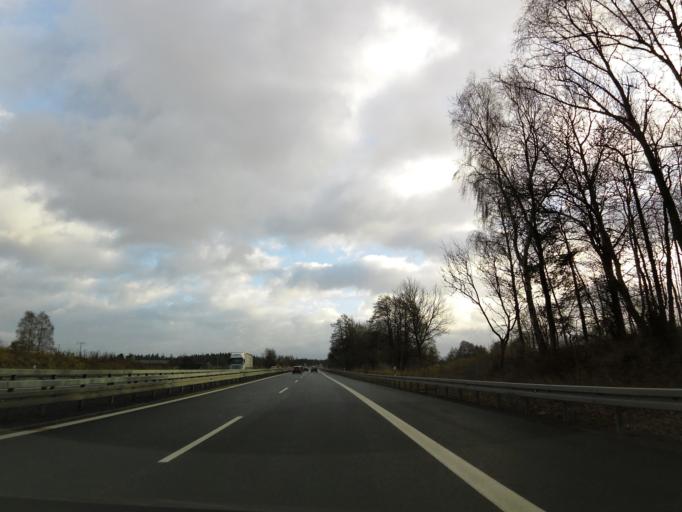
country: DE
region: Bavaria
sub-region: Upper Franconia
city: Thierstein
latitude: 50.0897
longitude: 12.1001
